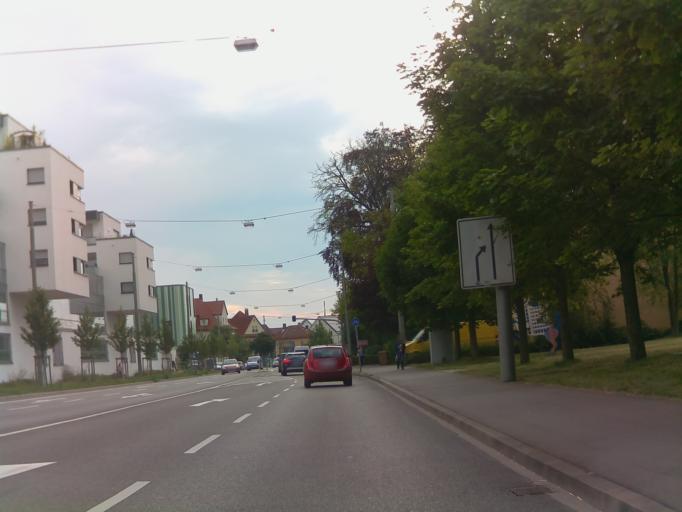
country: DE
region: Baden-Wuerttemberg
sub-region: Regierungsbezirk Stuttgart
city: Leinfelden-Echterdingen
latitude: 48.7281
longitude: 9.1361
